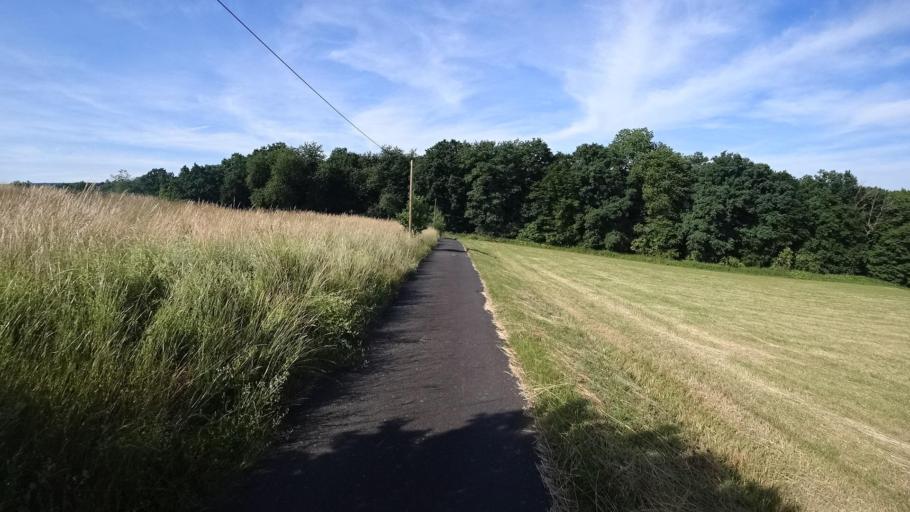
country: DE
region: Rheinland-Pfalz
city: Oberwambach
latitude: 50.6743
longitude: 7.6620
